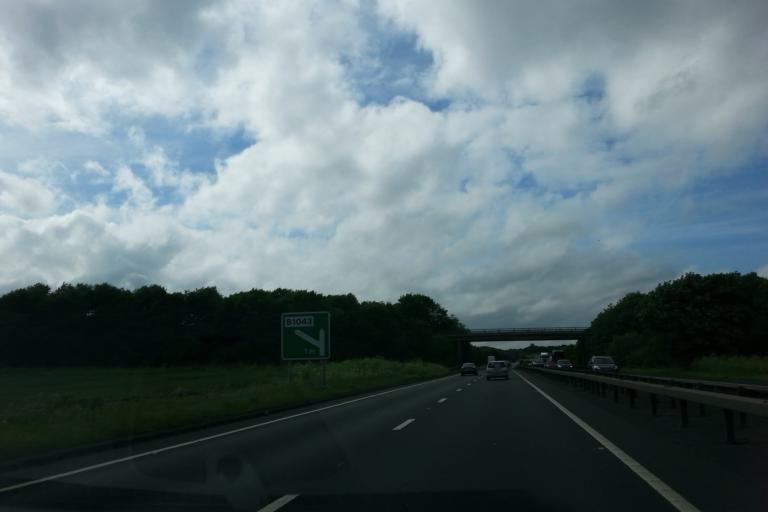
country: GB
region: England
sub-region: Cambridgeshire
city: Great Stukeley
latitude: 52.3555
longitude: -0.2300
